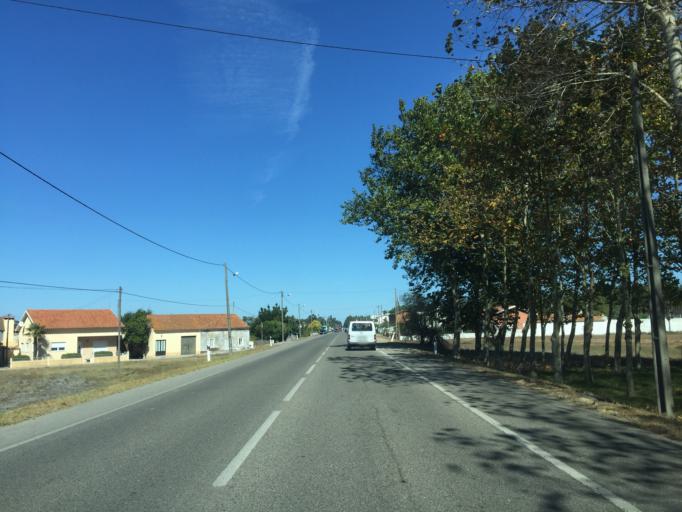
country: PT
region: Coimbra
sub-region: Figueira da Foz
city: Alhadas
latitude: 40.2784
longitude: -8.7727
